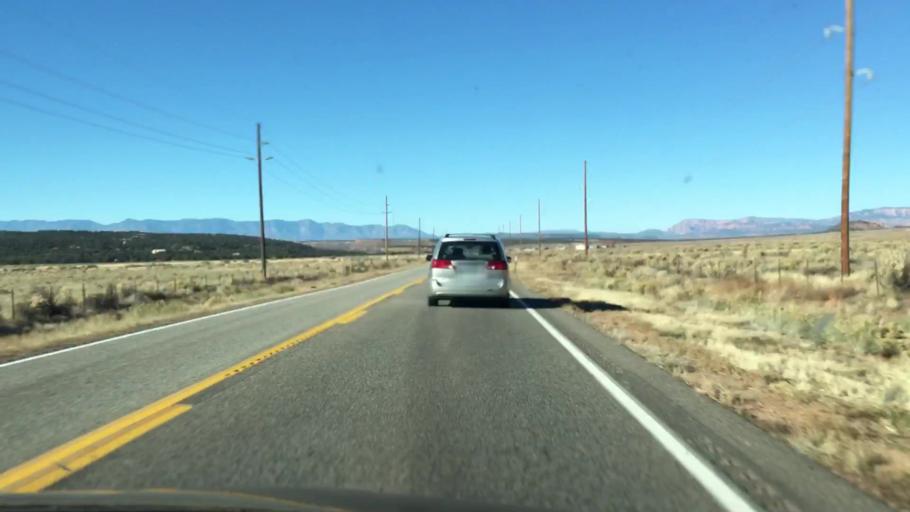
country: US
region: Arizona
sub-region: Mohave County
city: Colorado City
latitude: 37.0782
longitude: -113.1081
